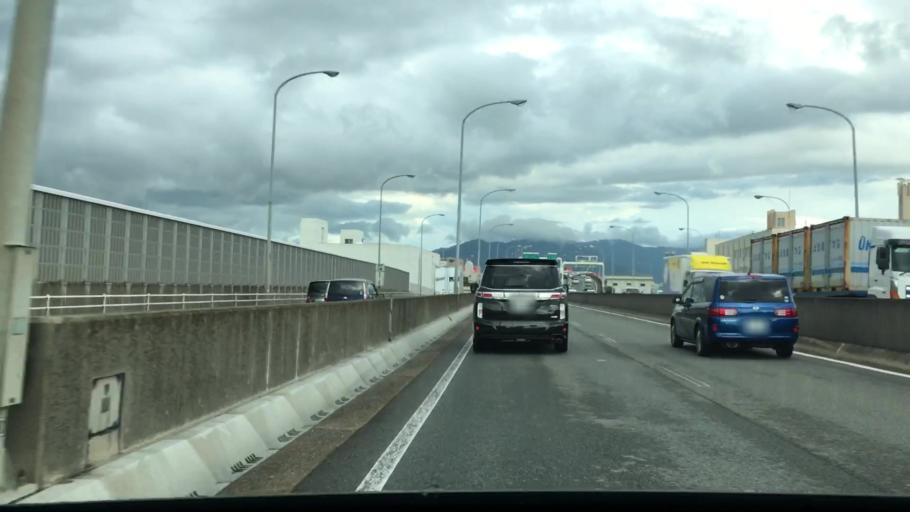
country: JP
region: Fukuoka
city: Fukuoka-shi
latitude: 33.6331
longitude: 130.4299
